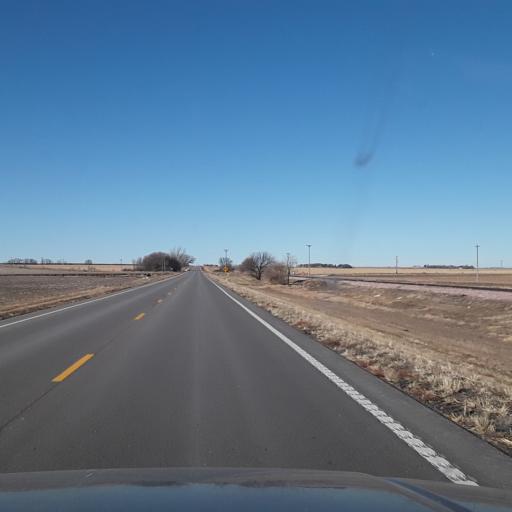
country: US
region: Nebraska
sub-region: Phelps County
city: Holdrege
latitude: 40.4941
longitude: -99.5460
